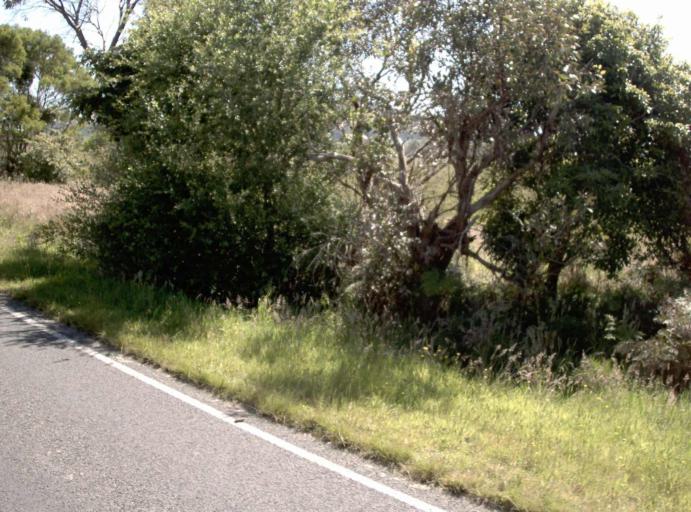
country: AU
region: Victoria
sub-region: Latrobe
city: Morwell
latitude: -38.6950
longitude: 146.1802
